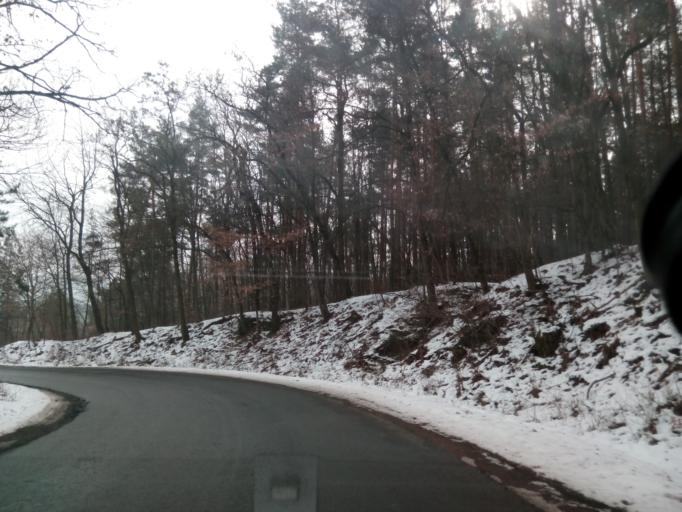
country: HU
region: Borsod-Abauj-Zemplen
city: Gonc
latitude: 48.4819
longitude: 21.3907
